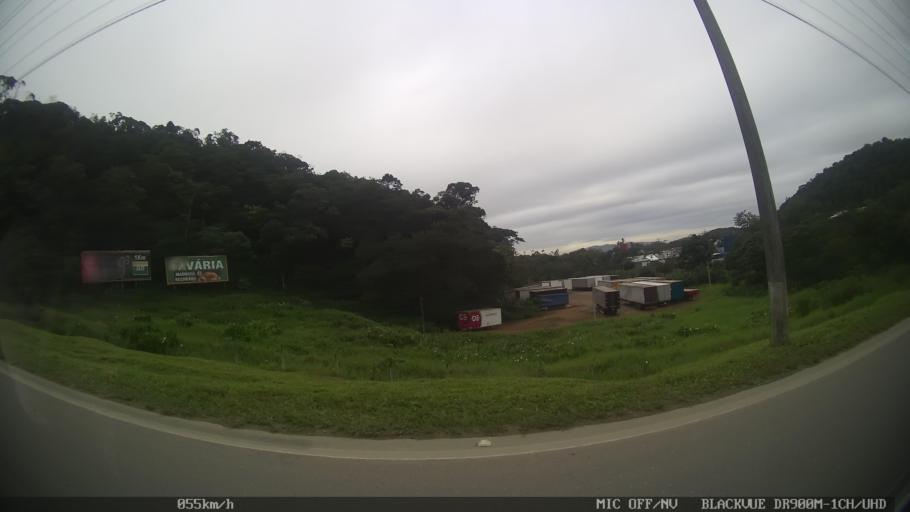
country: BR
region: Santa Catarina
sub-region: Joinville
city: Joinville
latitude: -26.2288
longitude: -48.9163
